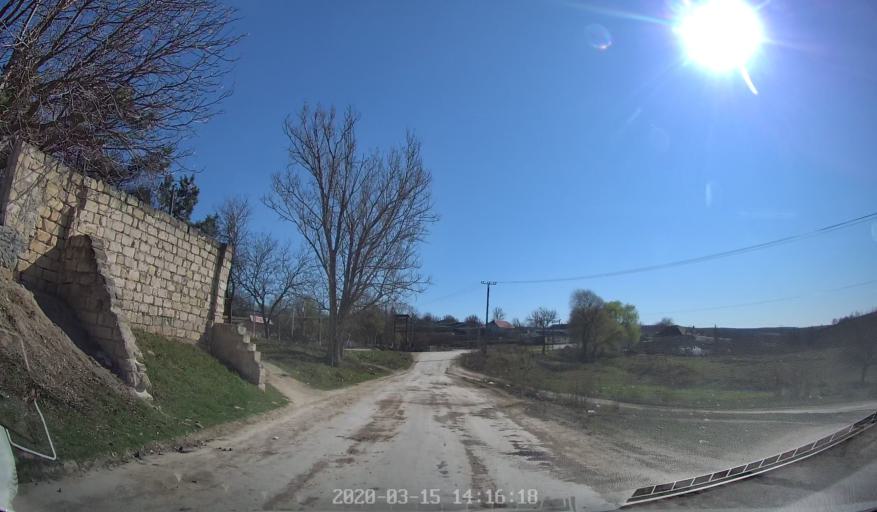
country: MD
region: Orhei
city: Orhei
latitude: 47.3108
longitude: 28.9320
